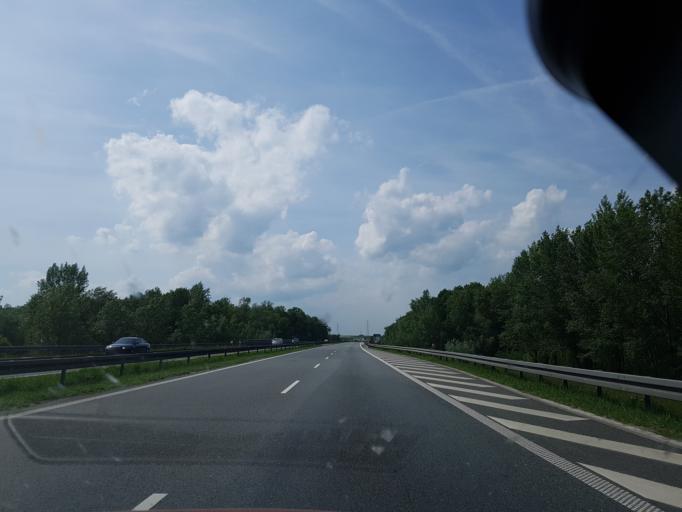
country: PL
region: Opole Voivodeship
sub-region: Powiat brzeski
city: Olszanka
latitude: 50.7267
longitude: 17.5156
